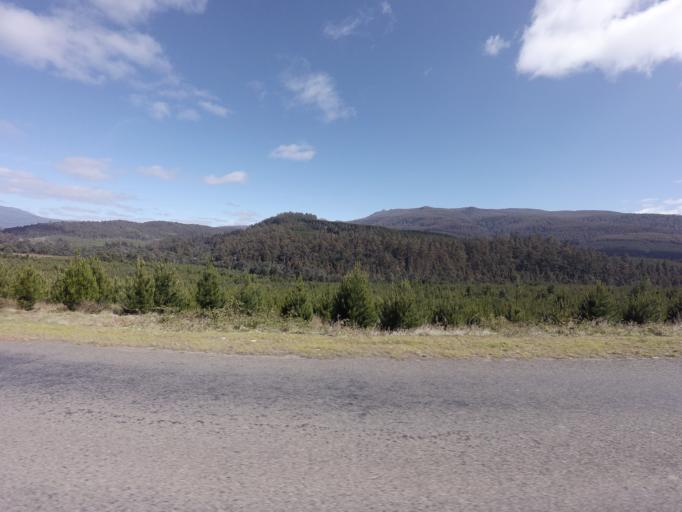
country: AU
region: Tasmania
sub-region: Derwent Valley
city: New Norfolk
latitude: -42.7447
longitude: 146.6546
